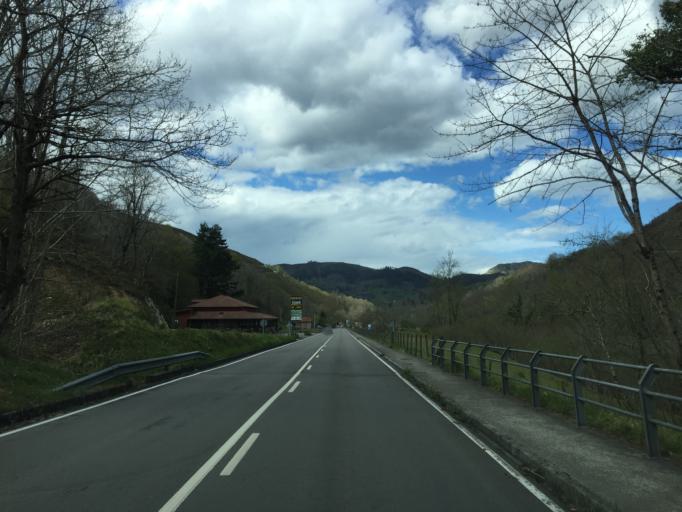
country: ES
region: Asturias
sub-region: Province of Asturias
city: Cangas de Onis
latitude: 43.3328
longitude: -5.0831
